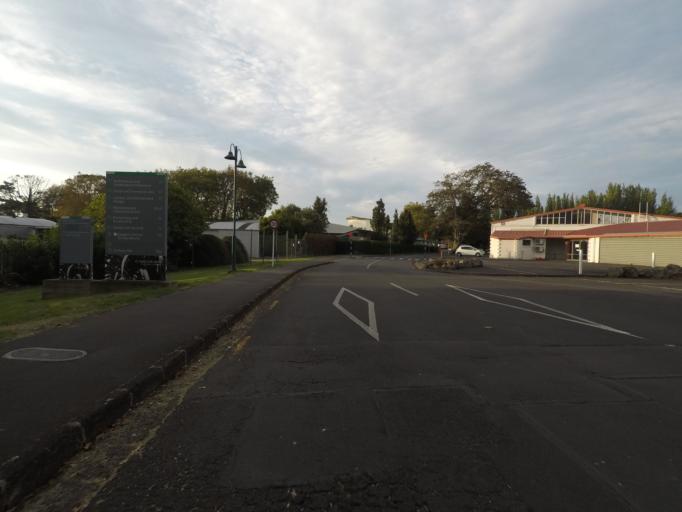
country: NZ
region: Auckland
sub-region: Auckland
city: Rosebank
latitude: -36.8767
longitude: 174.7067
